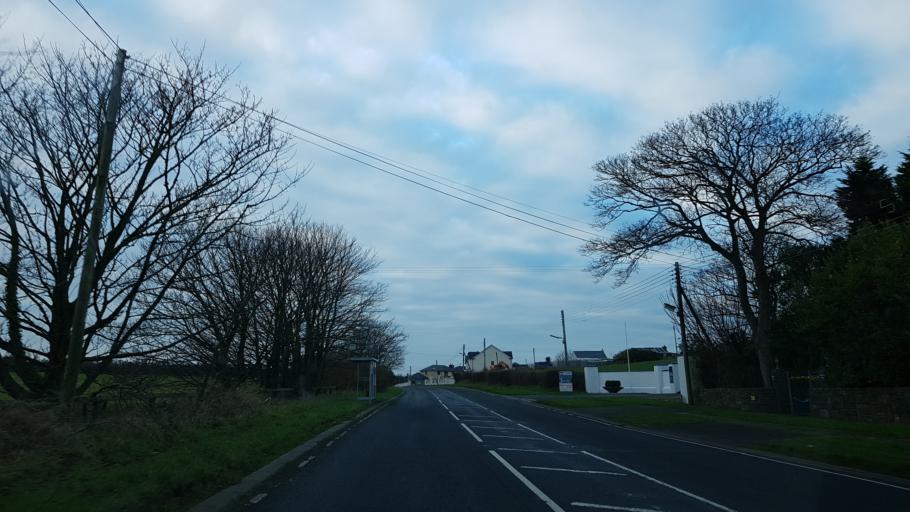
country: GB
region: Northern Ireland
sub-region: North Down District
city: Bangor
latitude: 54.6725
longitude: -5.6037
